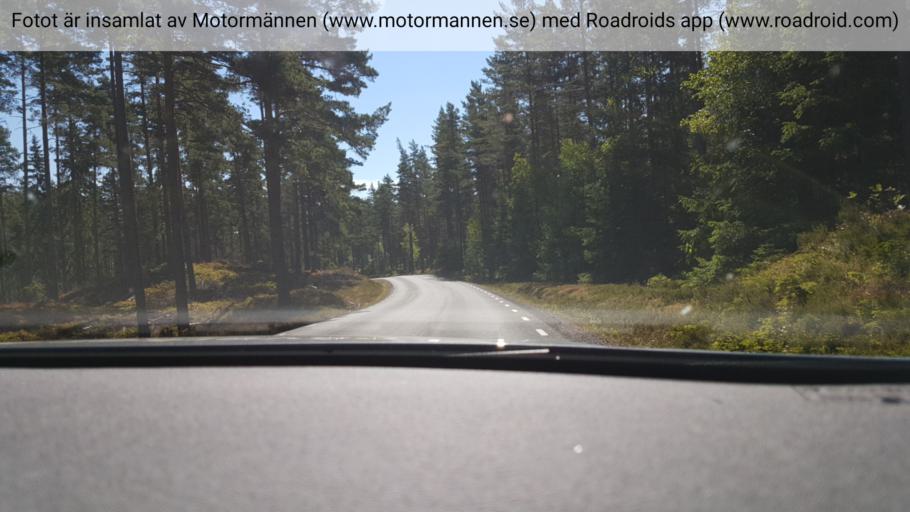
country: SE
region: Vaestra Goetaland
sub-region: Tidaholms Kommun
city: Tidaholm
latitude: 58.0999
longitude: 14.0890
